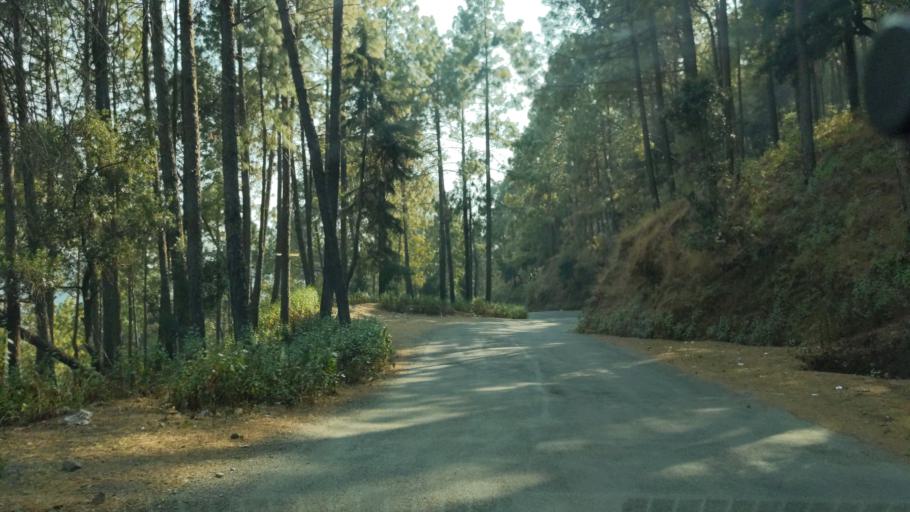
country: IN
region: Uttarakhand
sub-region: Naini Tal
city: Bhowali
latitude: 29.3944
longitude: 79.5392
